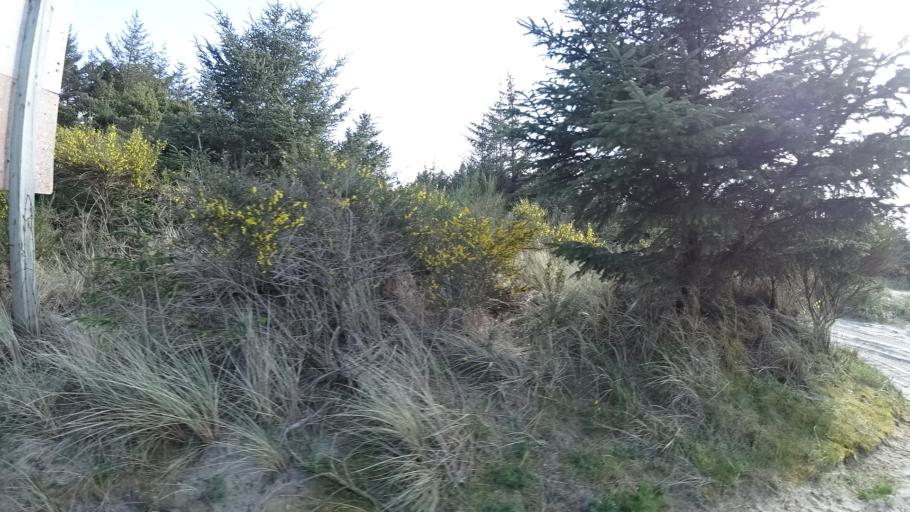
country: US
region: Oregon
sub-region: Douglas County
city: Reedsport
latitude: 43.7485
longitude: -124.1800
